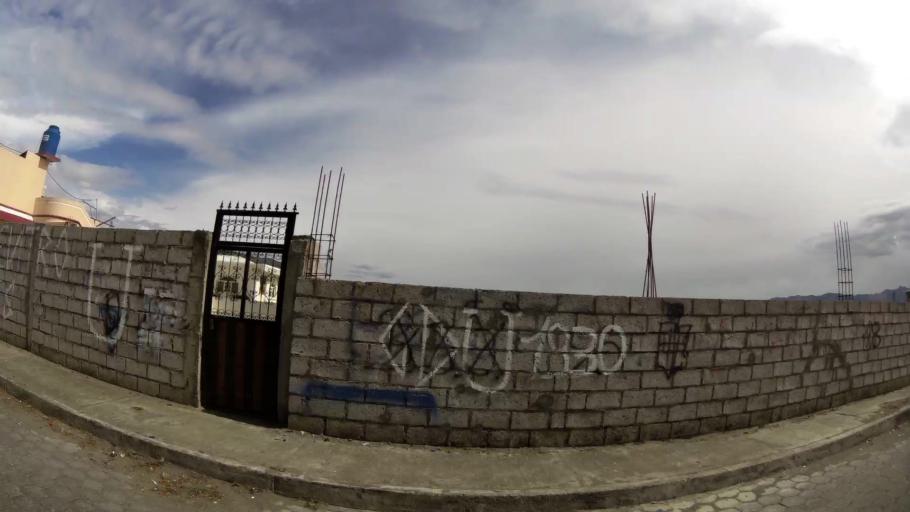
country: EC
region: Cotopaxi
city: Latacunga
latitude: -0.9349
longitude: -78.6090
